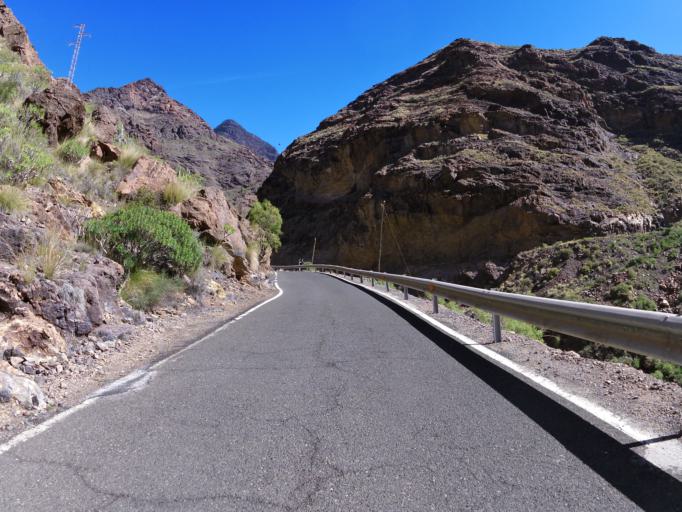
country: ES
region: Canary Islands
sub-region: Provincia de Las Palmas
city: San Nicolas
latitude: 27.9832
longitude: -15.7230
